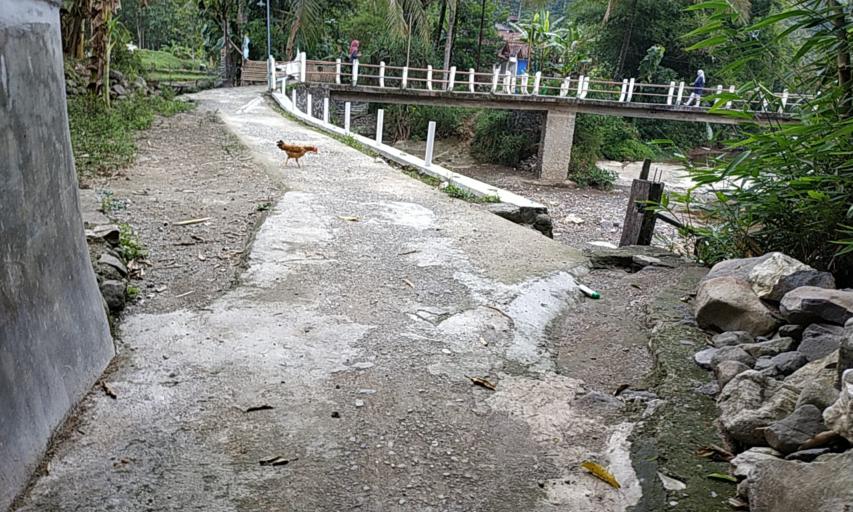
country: ID
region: Central Java
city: Gombong
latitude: -7.5846
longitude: 109.7149
